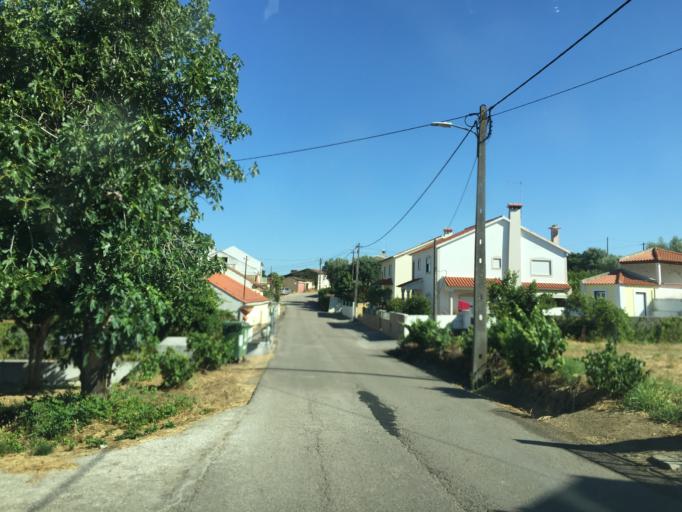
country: PT
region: Santarem
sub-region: Tomar
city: Tomar
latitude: 39.5992
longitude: -8.3264
